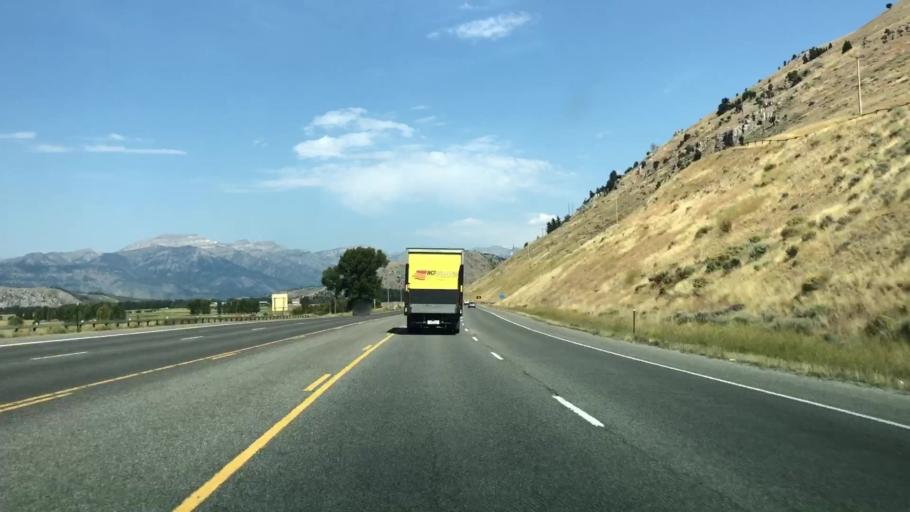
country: US
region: Wyoming
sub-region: Teton County
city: South Park
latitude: 43.4373
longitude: -110.7865
